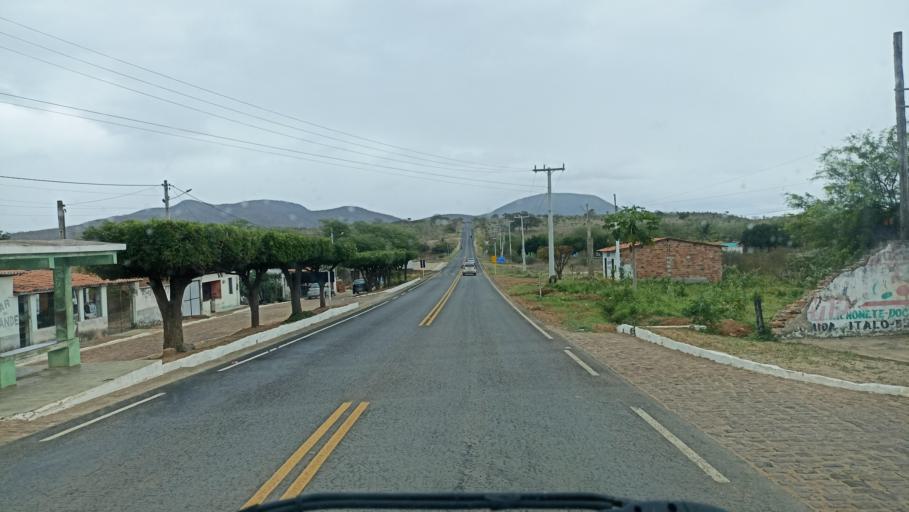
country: BR
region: Bahia
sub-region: Maracas
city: Maracas
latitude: -13.0486
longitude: -40.7470
